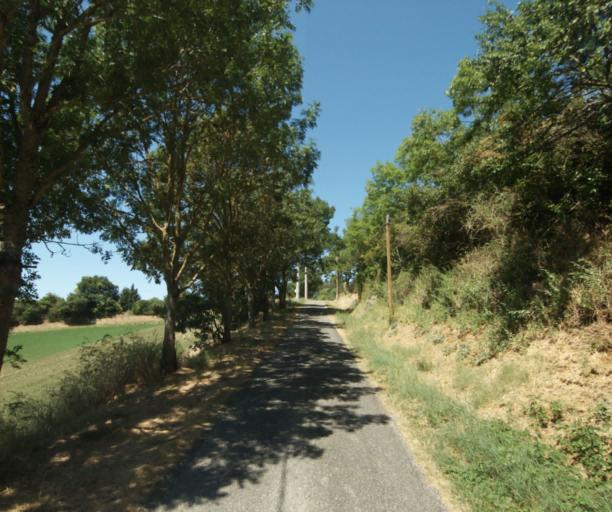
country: FR
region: Midi-Pyrenees
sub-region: Departement de la Haute-Garonne
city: Saint-Felix-Lauragais
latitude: 43.4925
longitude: 1.9289
